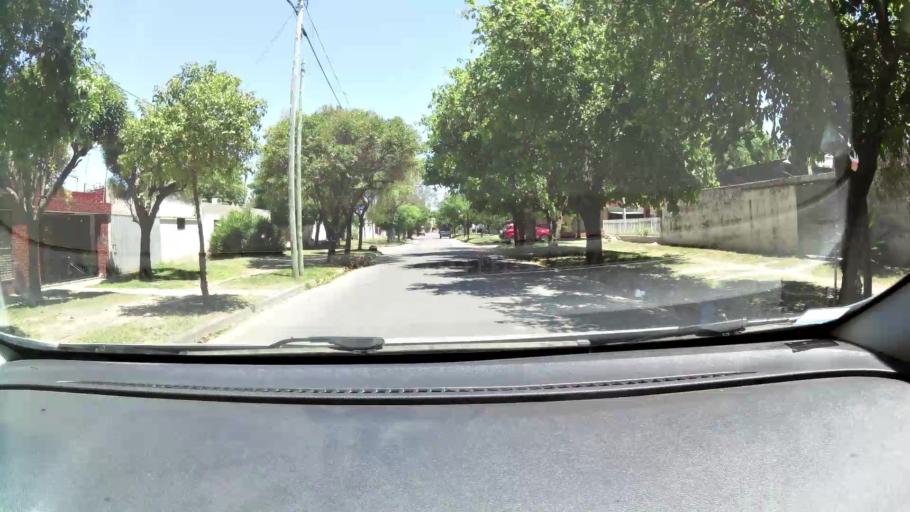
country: AR
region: Cordoba
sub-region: Departamento de Capital
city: Cordoba
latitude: -31.4354
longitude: -64.1256
